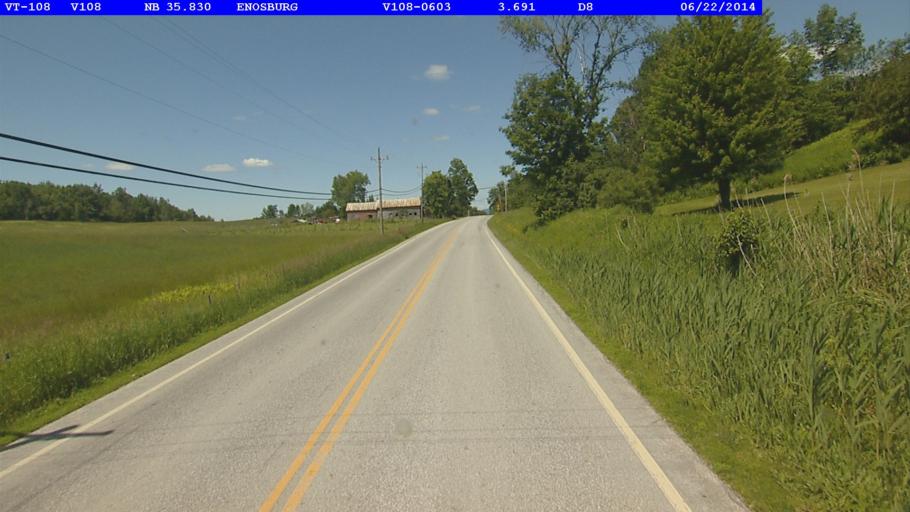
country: US
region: Vermont
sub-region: Franklin County
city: Enosburg Falls
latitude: 44.8888
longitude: -72.8026
